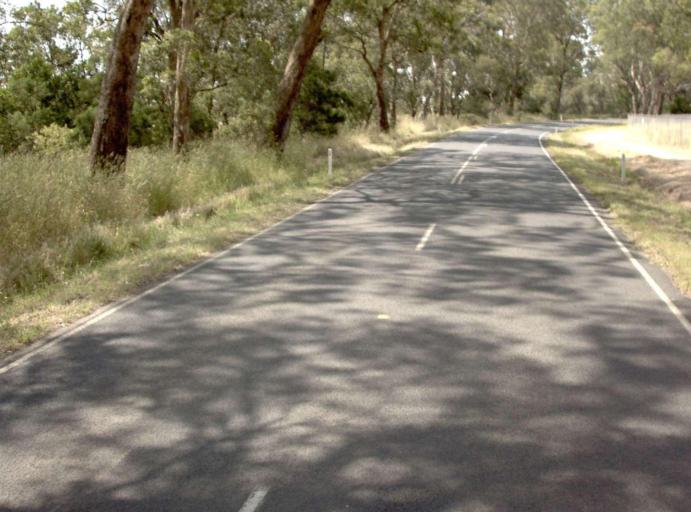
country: AU
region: Victoria
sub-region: Latrobe
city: Traralgon
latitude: -38.2609
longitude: 146.5468
